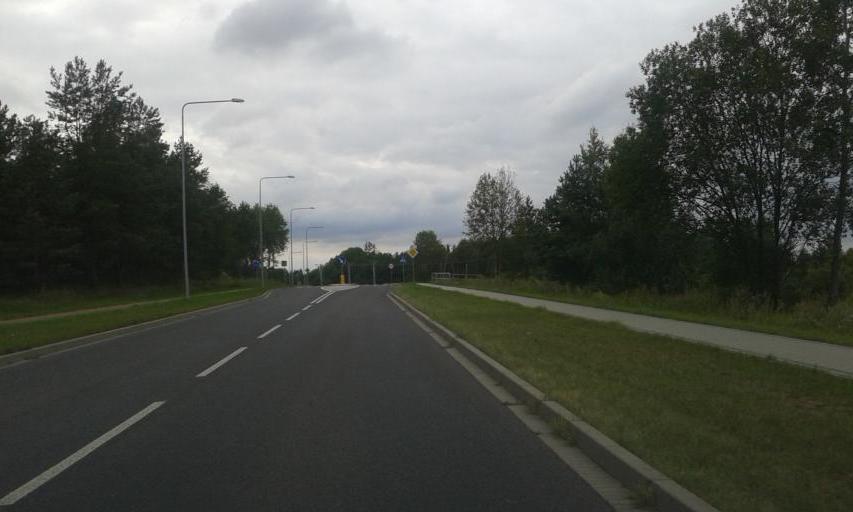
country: PL
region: West Pomeranian Voivodeship
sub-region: Powiat szczecinecki
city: Szczecinek
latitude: 53.7238
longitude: 16.6527
